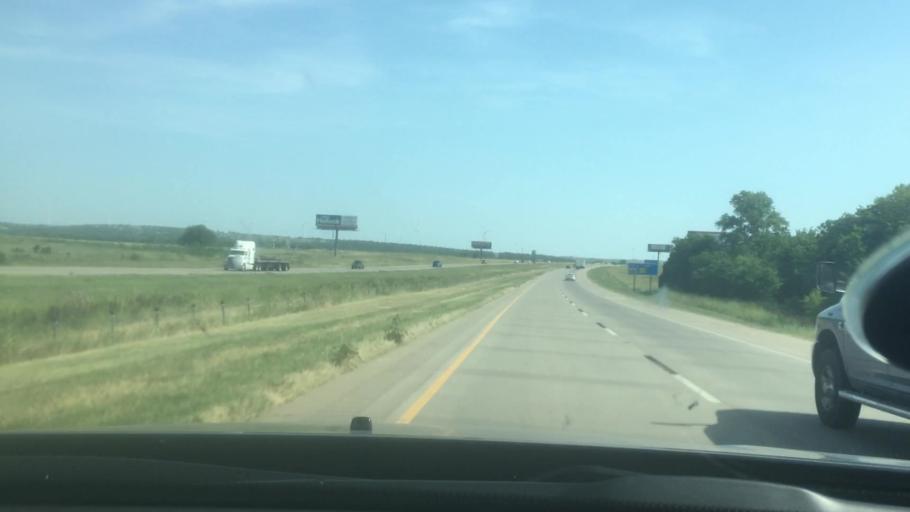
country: US
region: Oklahoma
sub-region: Carter County
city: Ardmore
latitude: 34.3226
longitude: -97.1554
